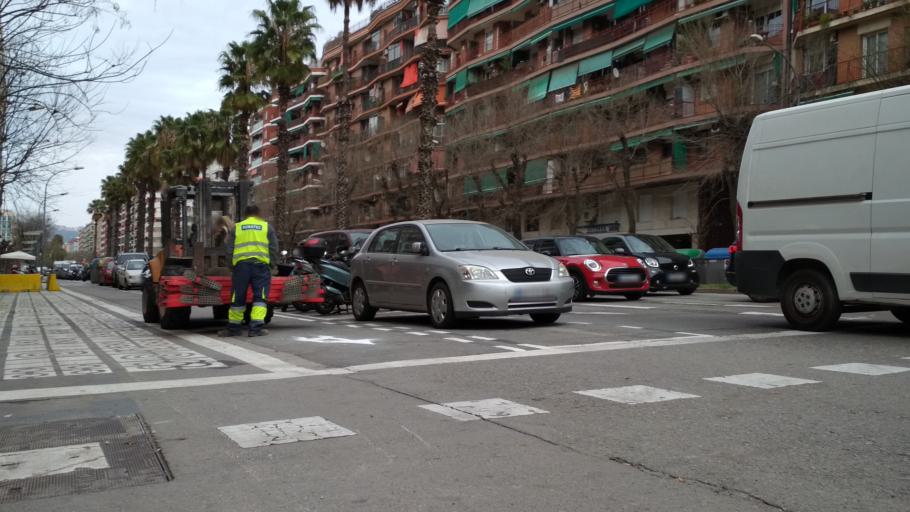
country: ES
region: Catalonia
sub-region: Provincia de Barcelona
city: Sants-Montjuic
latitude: 41.3585
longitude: 2.1401
